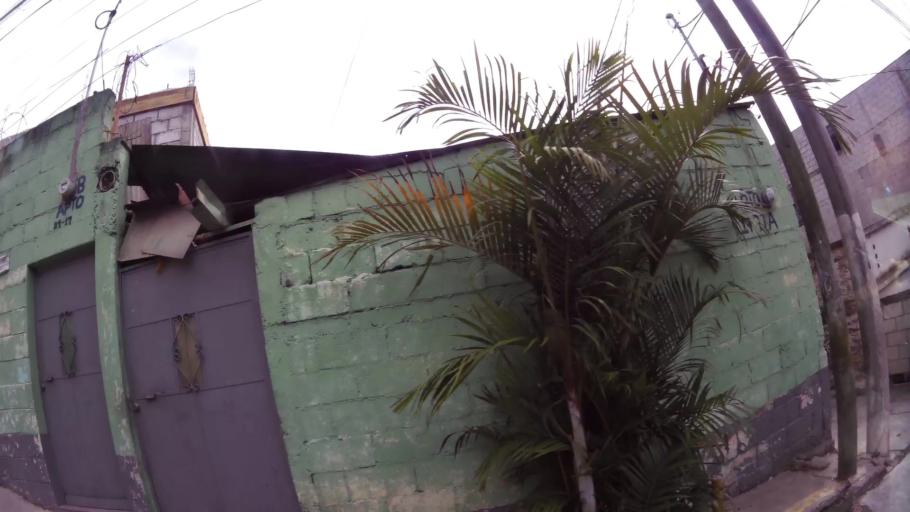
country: GT
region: Guatemala
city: Santa Catarina Pinula
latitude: 14.5682
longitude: -90.5342
